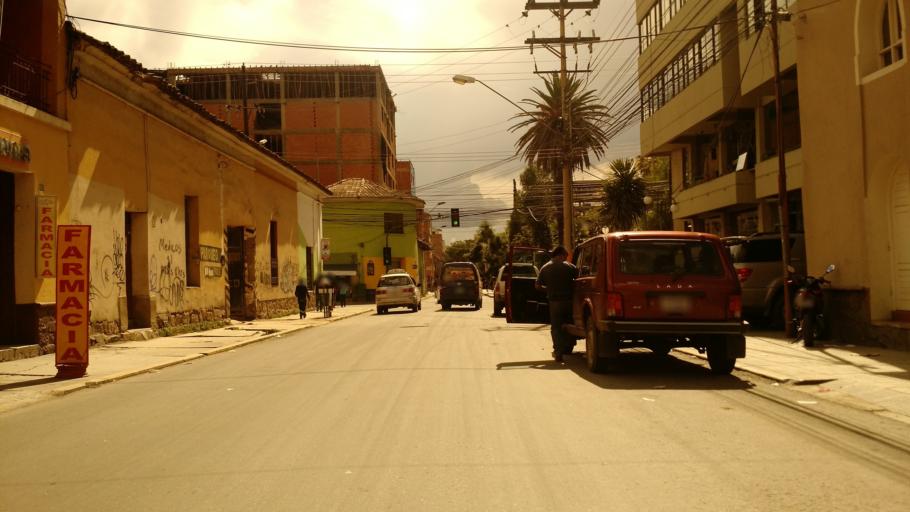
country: BO
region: Cochabamba
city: Cochabamba
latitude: -17.3919
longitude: -66.1493
